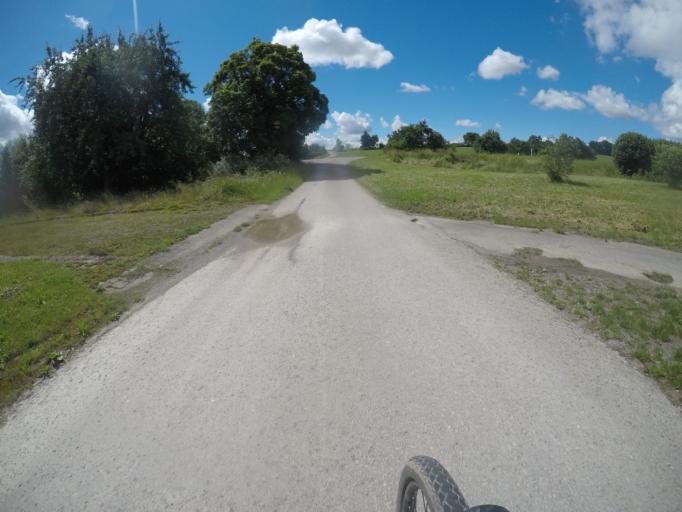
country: DE
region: Baden-Wuerttemberg
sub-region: Regierungsbezirk Stuttgart
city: Motzingen
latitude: 48.4975
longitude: 8.7495
